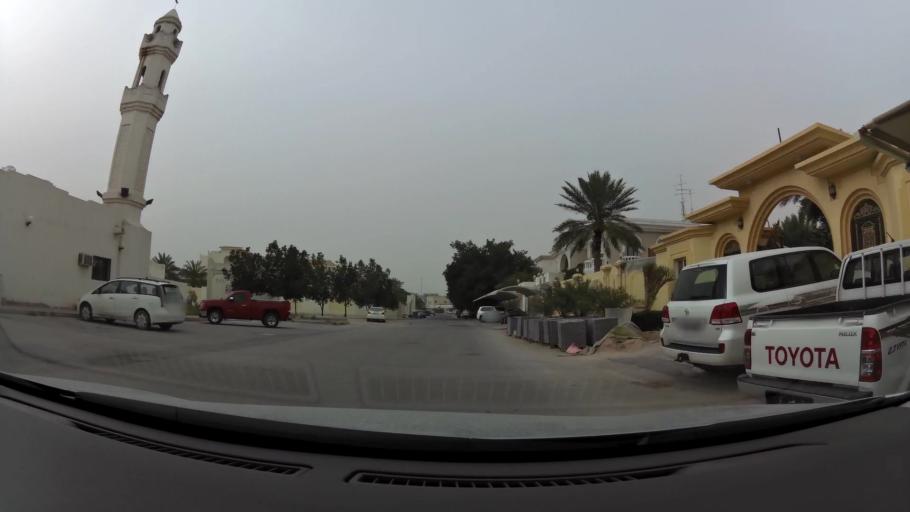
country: QA
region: Baladiyat ad Dawhah
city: Doha
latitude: 25.2570
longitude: 51.4935
